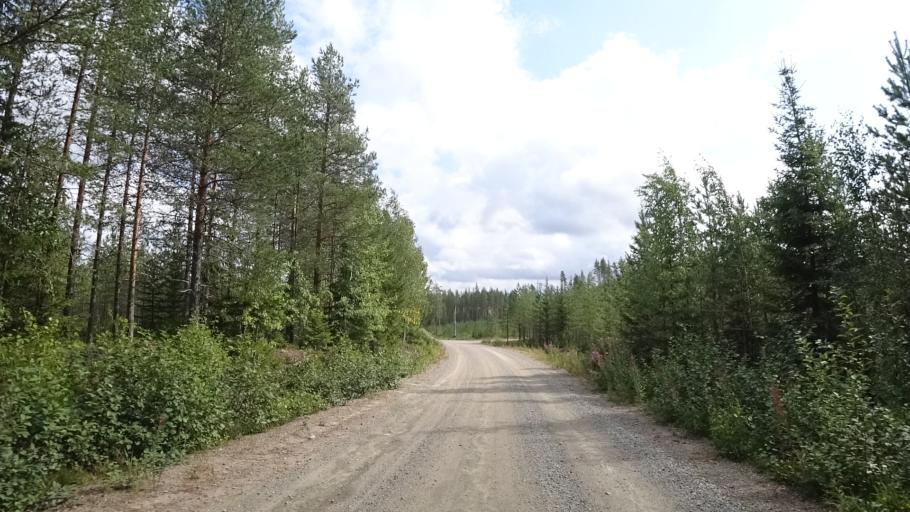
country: FI
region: North Karelia
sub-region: Joensuu
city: Ilomantsi
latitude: 62.9271
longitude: 31.3782
